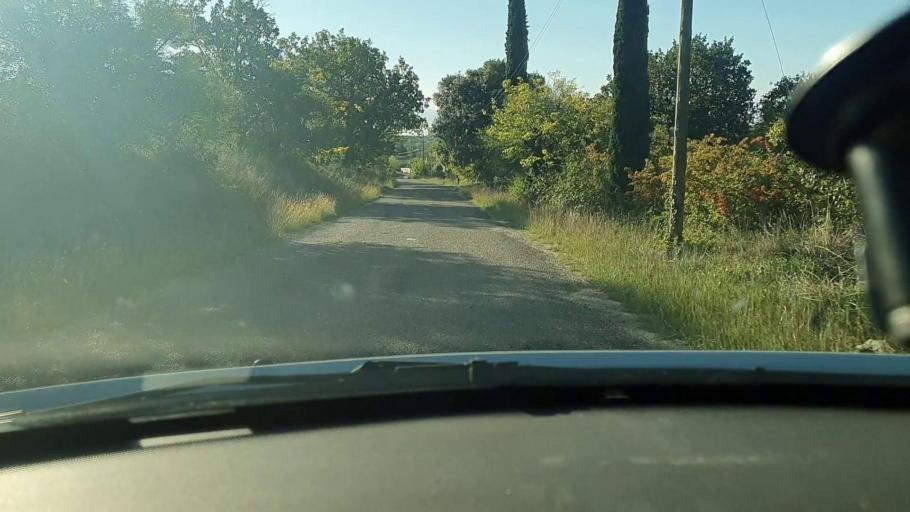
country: FR
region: Languedoc-Roussillon
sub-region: Departement du Gard
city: Barjac
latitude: 44.1890
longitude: 4.3238
